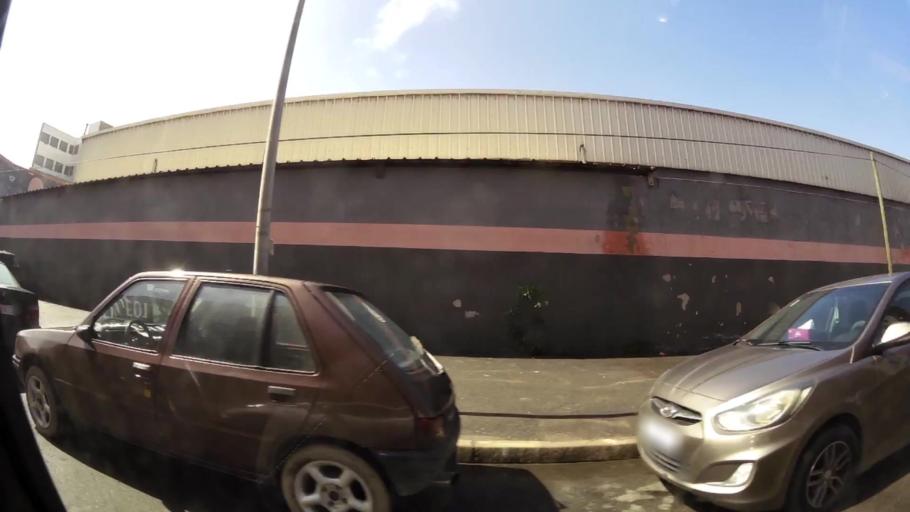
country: MA
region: Grand Casablanca
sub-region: Mediouna
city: Tit Mellil
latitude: 33.6269
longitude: -7.5102
